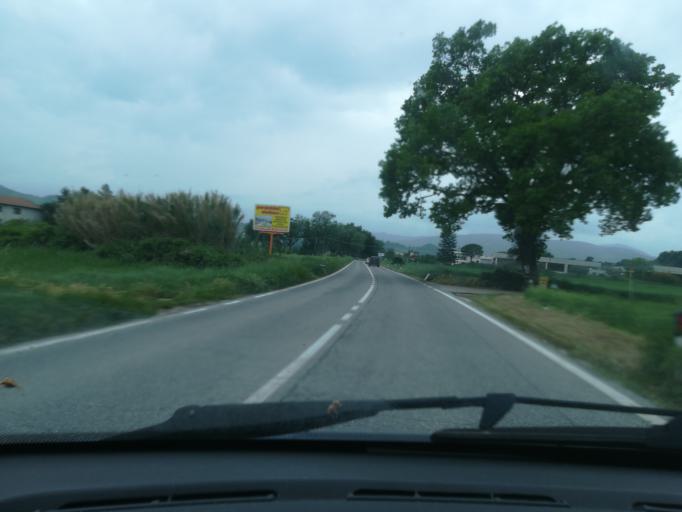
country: IT
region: The Marches
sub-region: Provincia di Macerata
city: San Severino Marche
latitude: 43.2541
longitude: 13.2319
